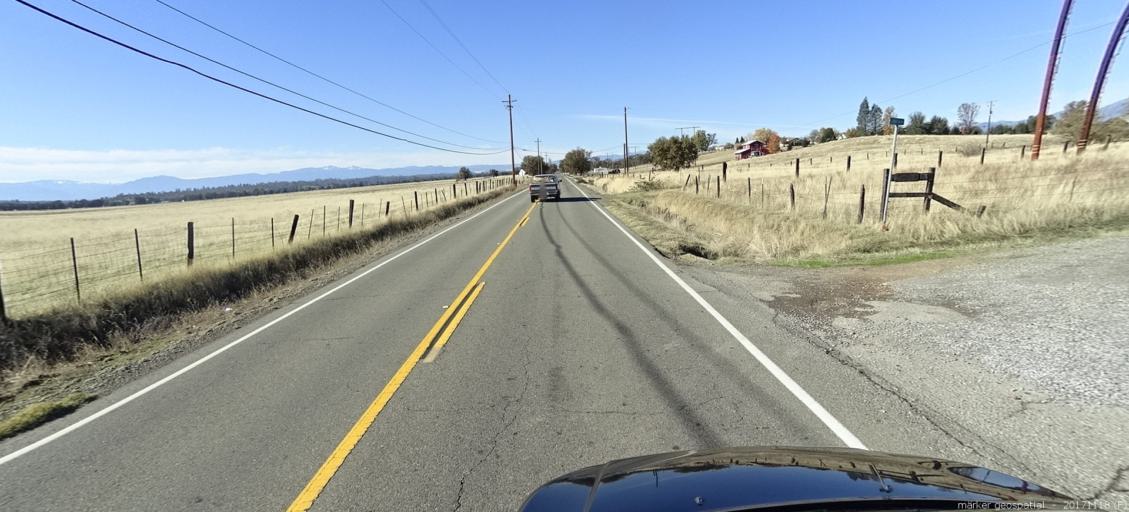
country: US
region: California
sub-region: Shasta County
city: Cottonwood
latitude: 40.3887
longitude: -122.3900
